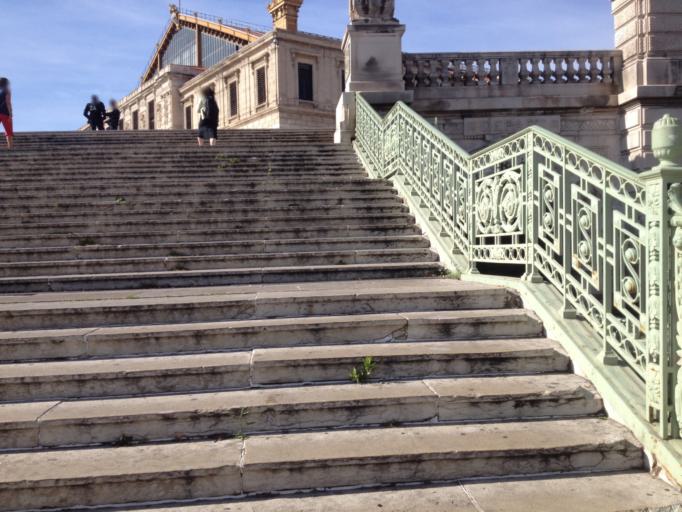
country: FR
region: Provence-Alpes-Cote d'Azur
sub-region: Departement des Bouches-du-Rhone
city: Marseille 03
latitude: 43.3017
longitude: 5.3801
